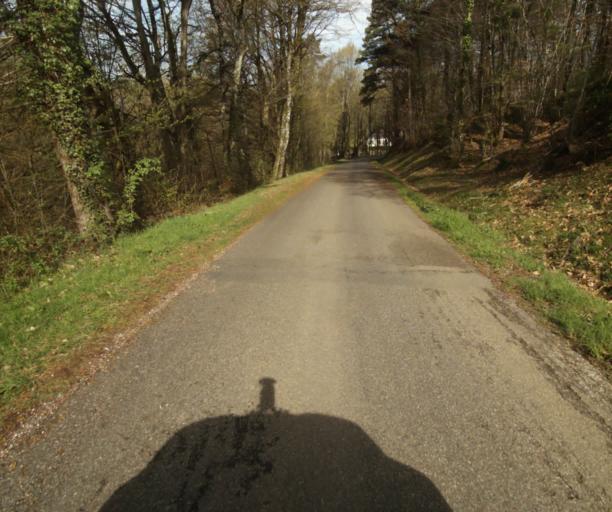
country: FR
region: Limousin
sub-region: Departement de la Correze
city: Laguenne
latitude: 45.2591
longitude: 1.8123
